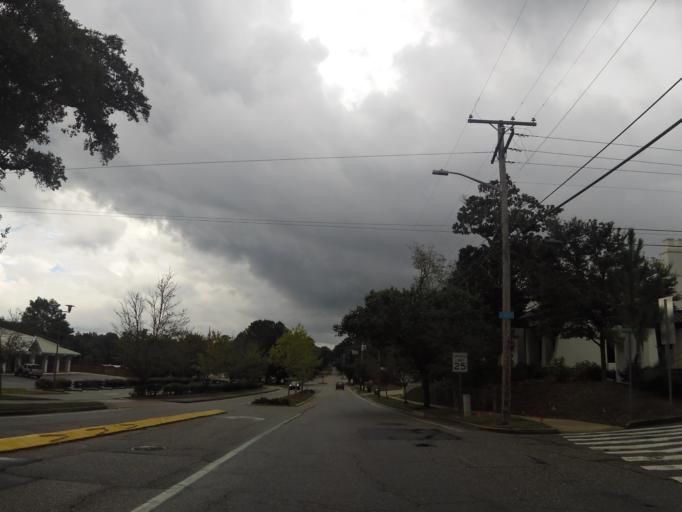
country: US
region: Alabama
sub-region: Baldwin County
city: Fairhope
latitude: 30.5230
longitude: -87.9006
